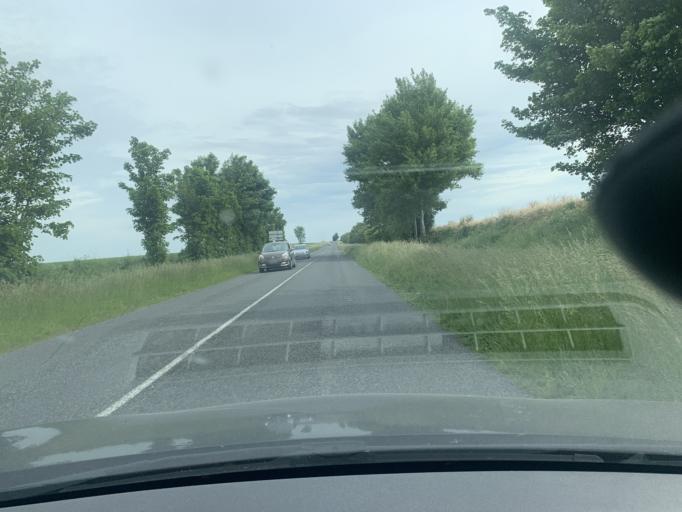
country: FR
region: Nord-Pas-de-Calais
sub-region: Departement du Nord
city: Rumilly-en-Cambresis
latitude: 50.1363
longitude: 3.2003
